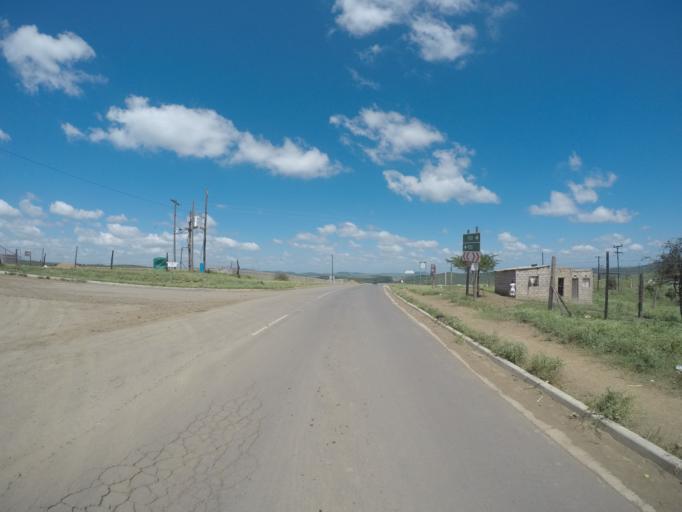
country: ZA
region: KwaZulu-Natal
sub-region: uThungulu District Municipality
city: Empangeni
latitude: -28.6065
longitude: 31.7461
